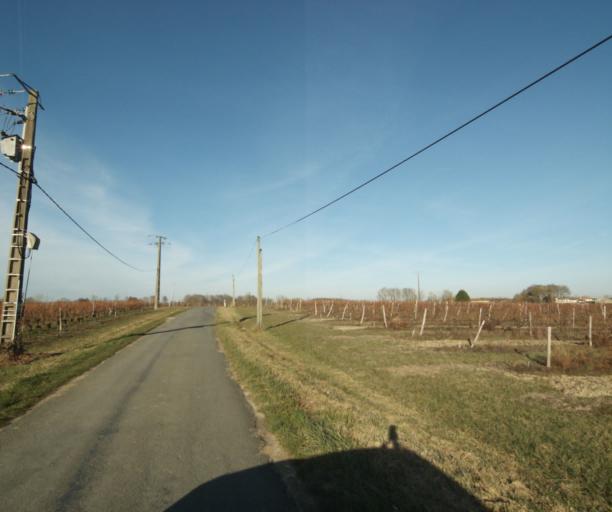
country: FR
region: Poitou-Charentes
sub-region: Departement de la Charente-Maritime
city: Burie
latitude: 45.7851
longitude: -0.4174
